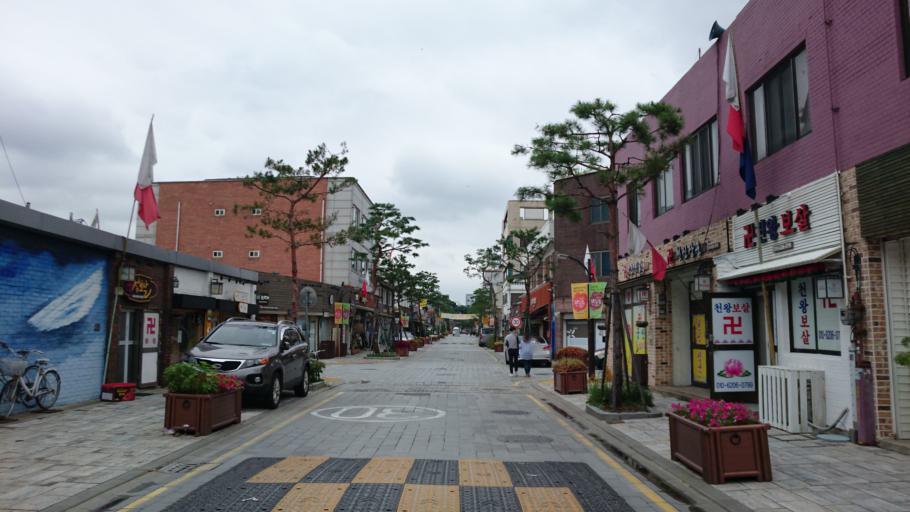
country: KR
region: Gyeonggi-do
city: Suwon-si
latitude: 37.2853
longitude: 127.0126
